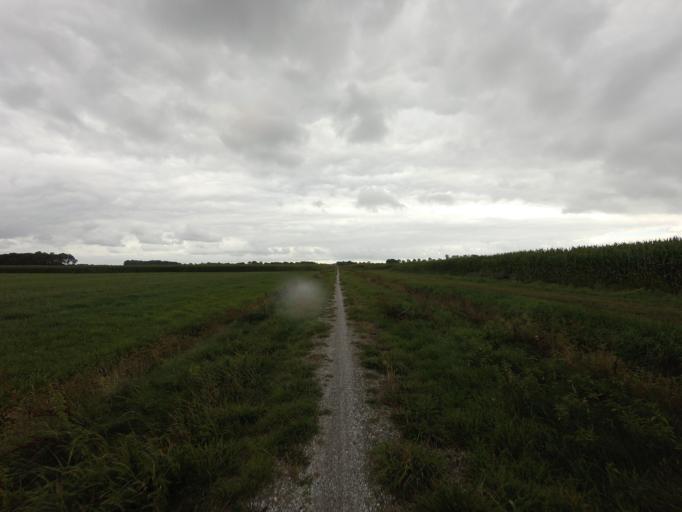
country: NL
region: Friesland
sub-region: Gemeente Weststellingwerf
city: Noordwolde
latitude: 52.9419
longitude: 6.1860
